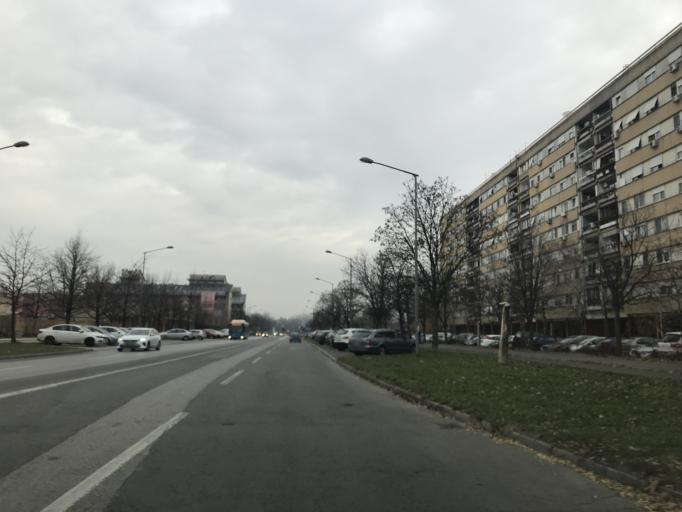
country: RS
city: Veternik
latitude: 45.2519
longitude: 19.7968
